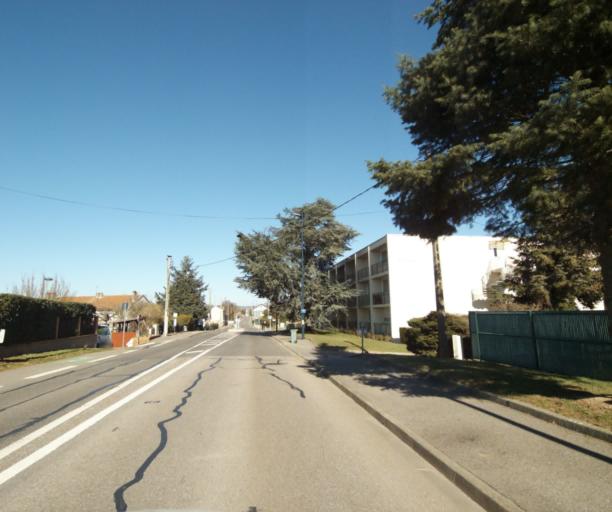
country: FR
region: Lorraine
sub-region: Departement de Meurthe-et-Moselle
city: Heillecourt
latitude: 48.6586
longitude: 6.2064
